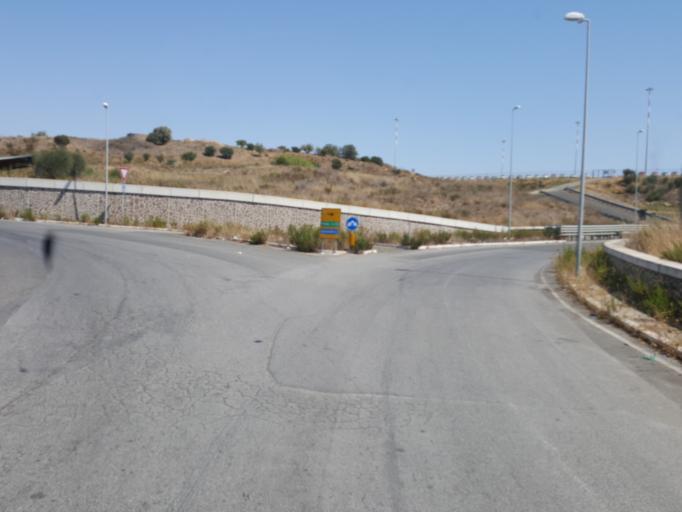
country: IT
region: Latium
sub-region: Citta metropolitana di Roma Capitale
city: Aurelia
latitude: 42.1243
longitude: 11.7782
